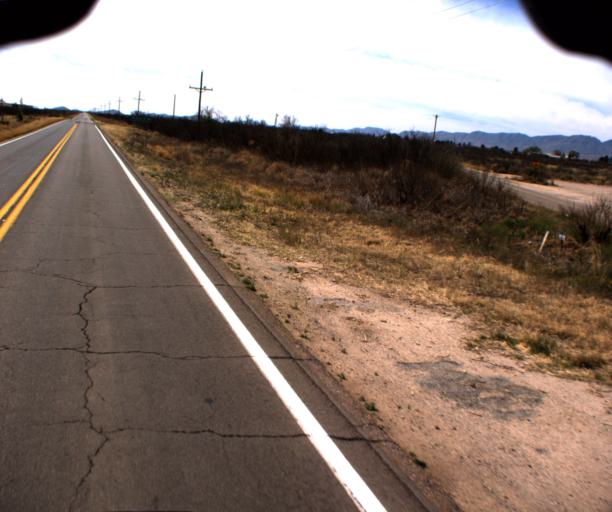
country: US
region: Arizona
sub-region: Cochise County
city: Willcox
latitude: 32.0066
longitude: -109.8643
